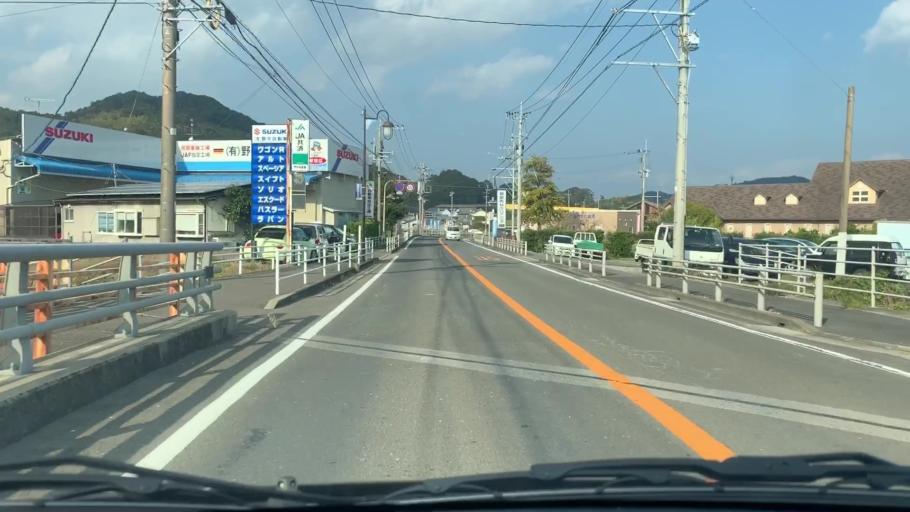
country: JP
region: Nagasaki
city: Togitsu
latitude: 32.9439
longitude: 129.7822
